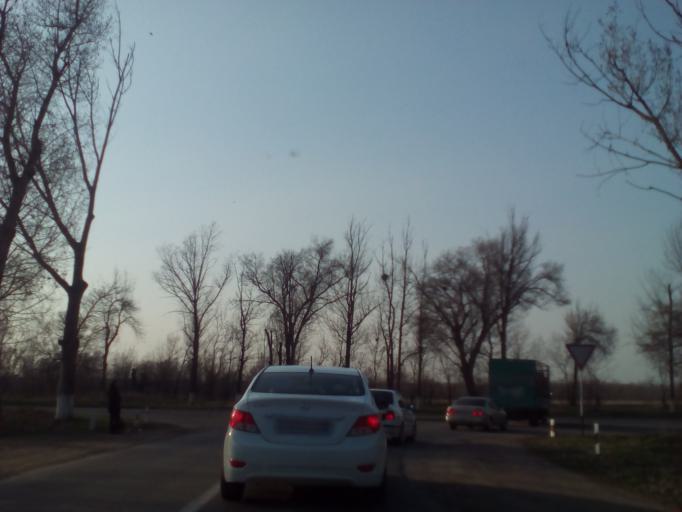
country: KZ
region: Almaty Oblysy
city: Burunday
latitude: 43.1823
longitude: 76.5143
